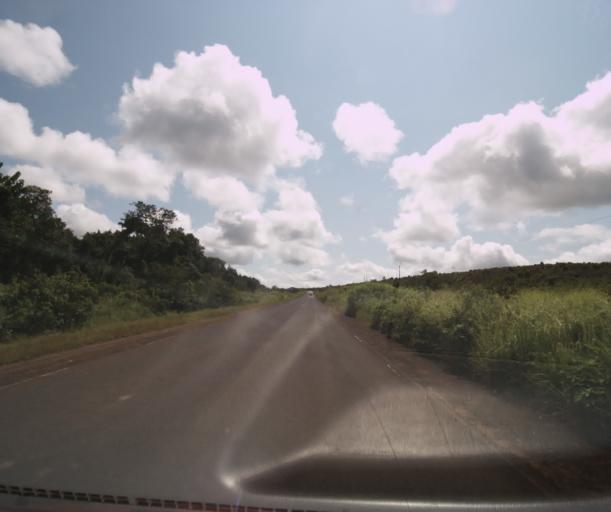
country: CM
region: West
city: Foumban
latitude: 5.6993
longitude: 10.8251
